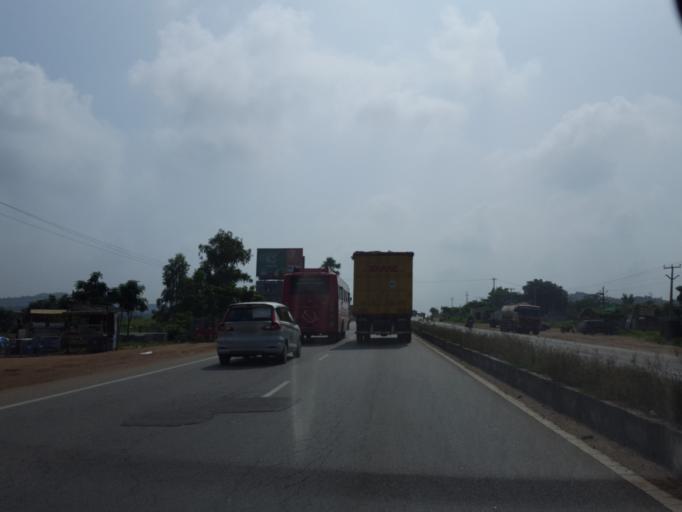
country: IN
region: Telangana
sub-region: Rangareddi
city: Ghatkesar
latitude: 17.2898
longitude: 78.7668
